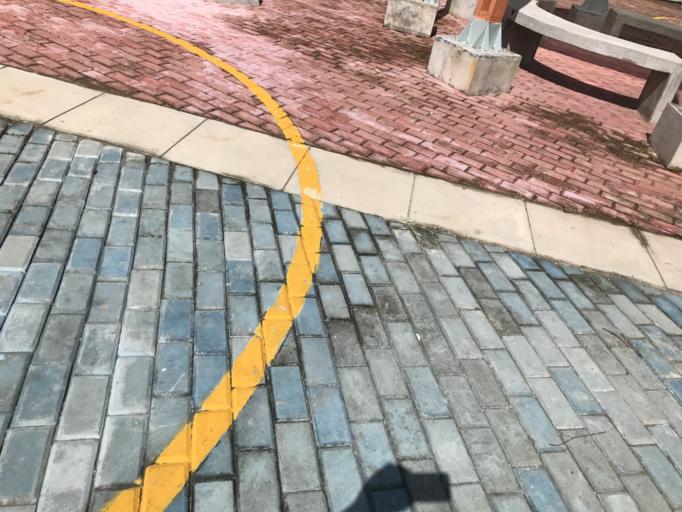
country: PE
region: Loreto
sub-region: Provincia de Maynas
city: Iquitos
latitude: -3.8125
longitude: -73.3177
